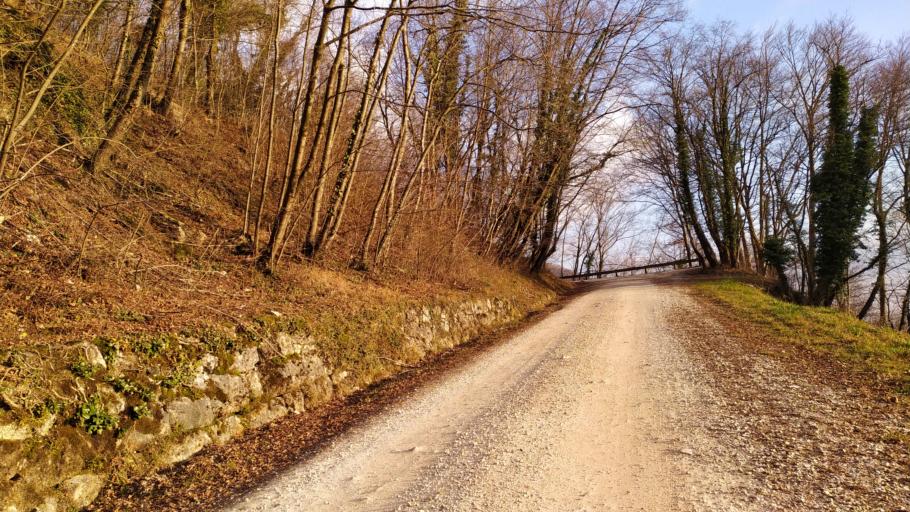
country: IT
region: Veneto
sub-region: Provincia di Vicenza
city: Velo d'Astico
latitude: 45.7622
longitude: 11.3694
